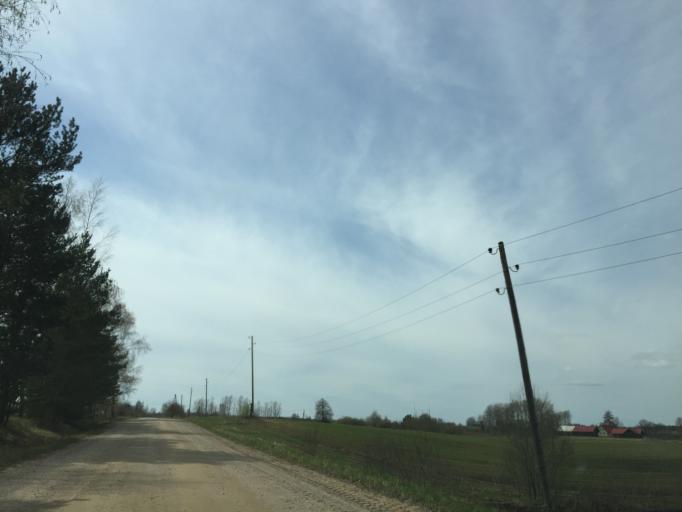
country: LV
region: Ludzas Rajons
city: Ludza
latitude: 56.5460
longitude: 27.5289
